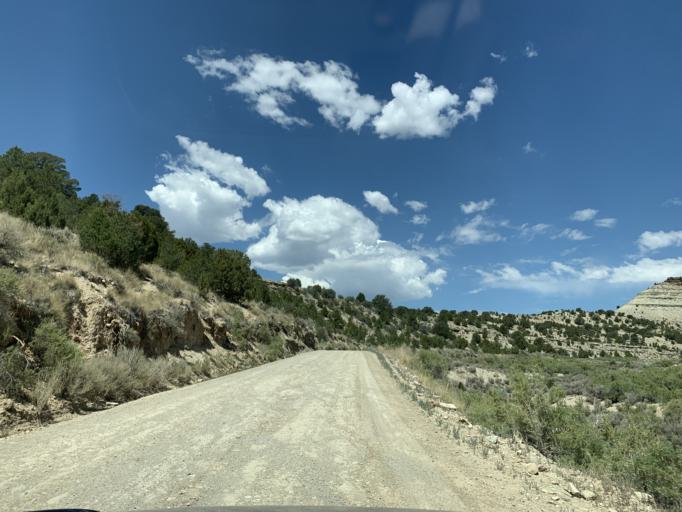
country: US
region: Utah
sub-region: Carbon County
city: East Carbon City
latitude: 39.8470
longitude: -110.2518
